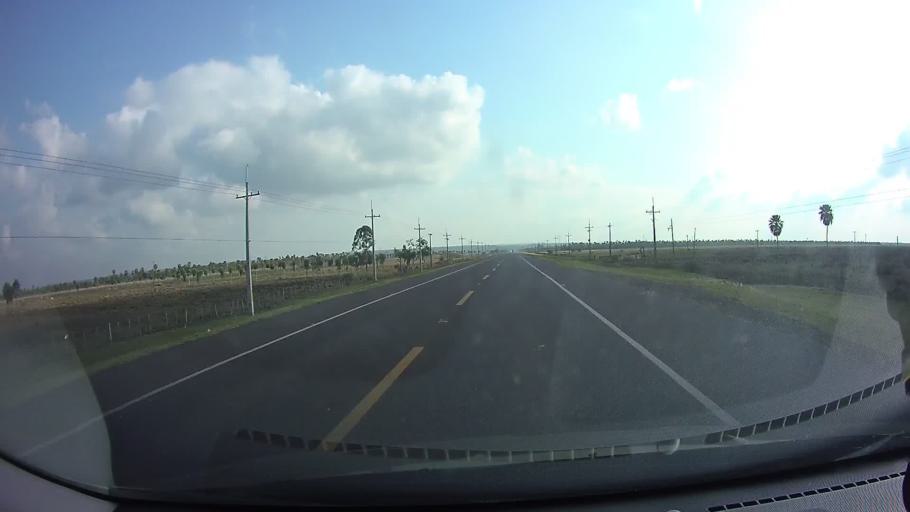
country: PY
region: Cordillera
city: Emboscada
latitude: -25.0720
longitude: -57.2595
